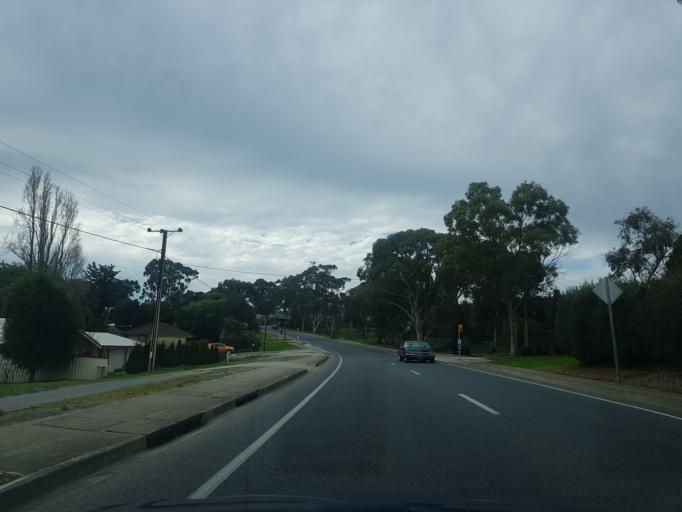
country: AU
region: South Australia
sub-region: Tea Tree Gully
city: Hope Valley
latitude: -34.8492
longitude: 138.7155
